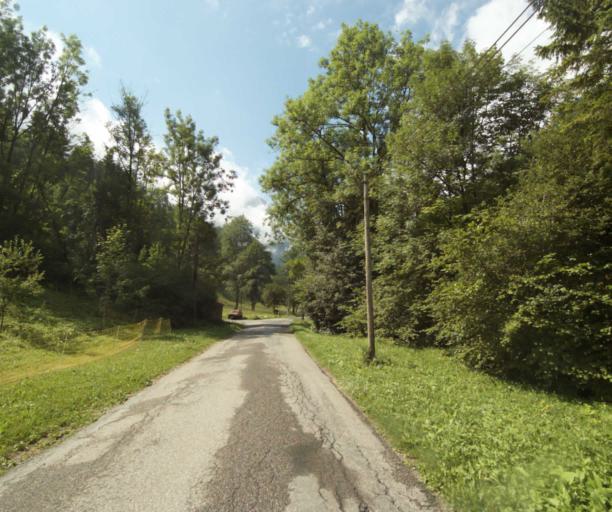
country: FR
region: Rhone-Alpes
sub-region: Departement de la Haute-Savoie
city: Thones
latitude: 45.8685
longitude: 6.2871
